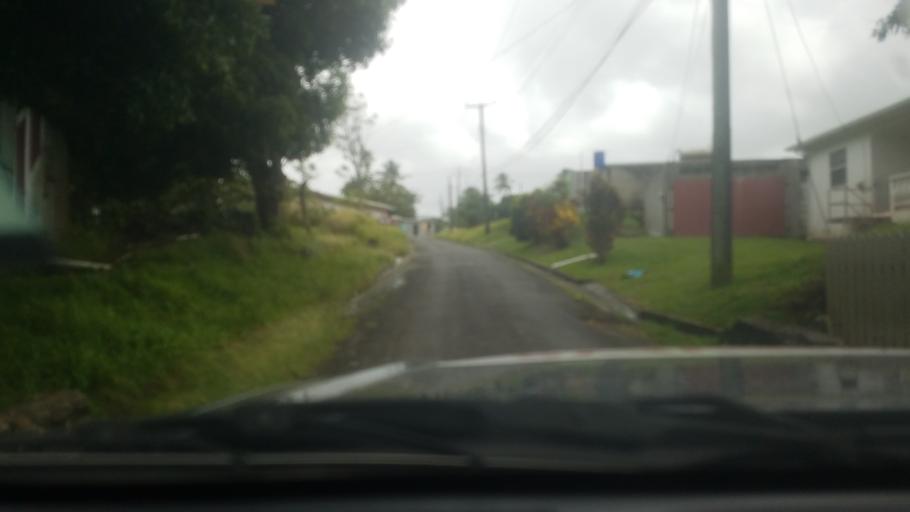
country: LC
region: Laborie Quarter
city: Laborie
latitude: 13.7776
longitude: -61.0001
